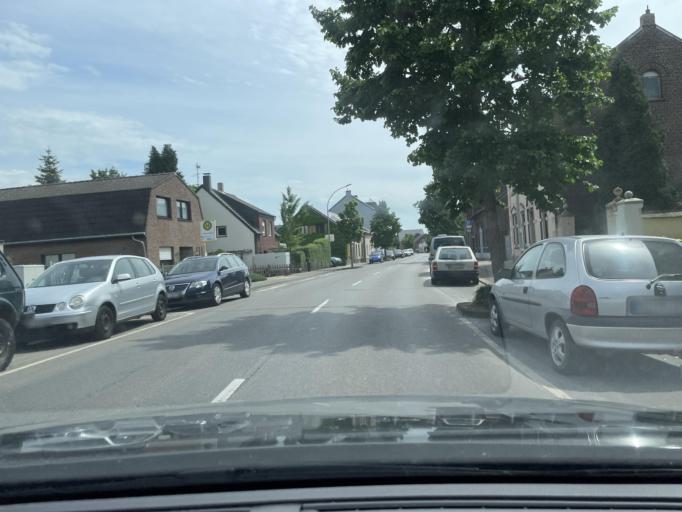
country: DE
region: North Rhine-Westphalia
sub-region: Regierungsbezirk Dusseldorf
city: Schwalmtal
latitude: 51.2076
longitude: 6.3330
